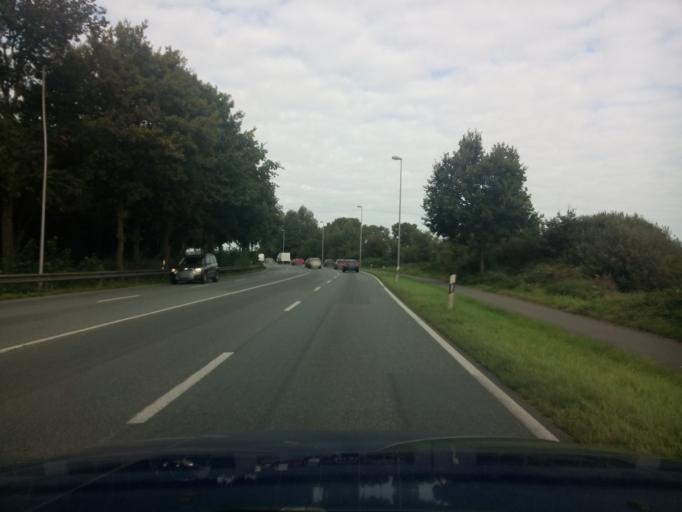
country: DE
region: Lower Saxony
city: Lilienthal
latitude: 53.1134
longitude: 8.8794
